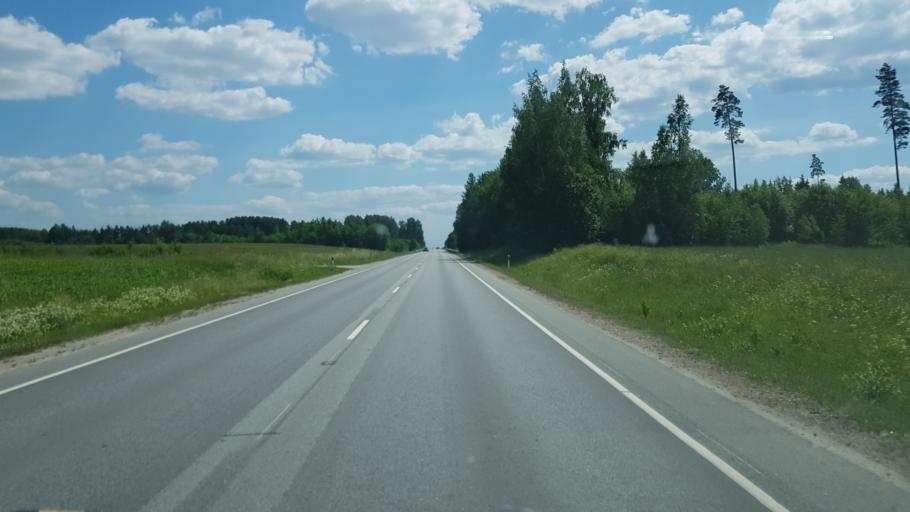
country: EE
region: Vorumaa
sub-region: Voru linn
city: Voru
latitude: 57.8991
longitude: 26.8402
